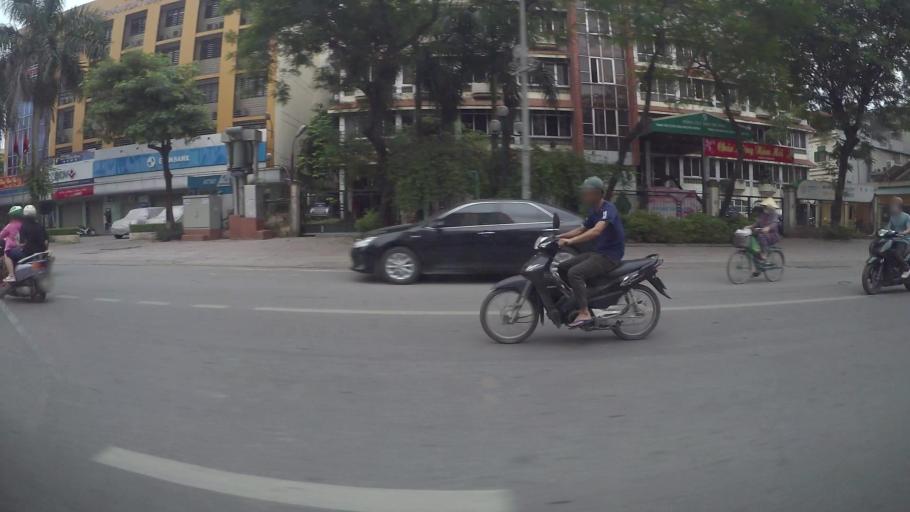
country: VN
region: Ha Noi
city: Hoan Kiem
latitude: 21.0490
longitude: 105.8828
